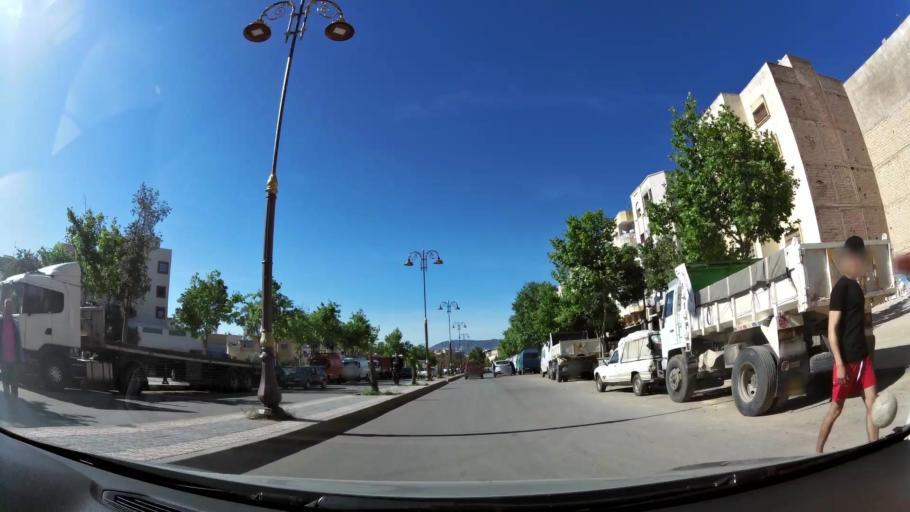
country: MA
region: Fes-Boulemane
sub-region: Fes
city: Fes
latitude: 34.0176
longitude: -4.9704
